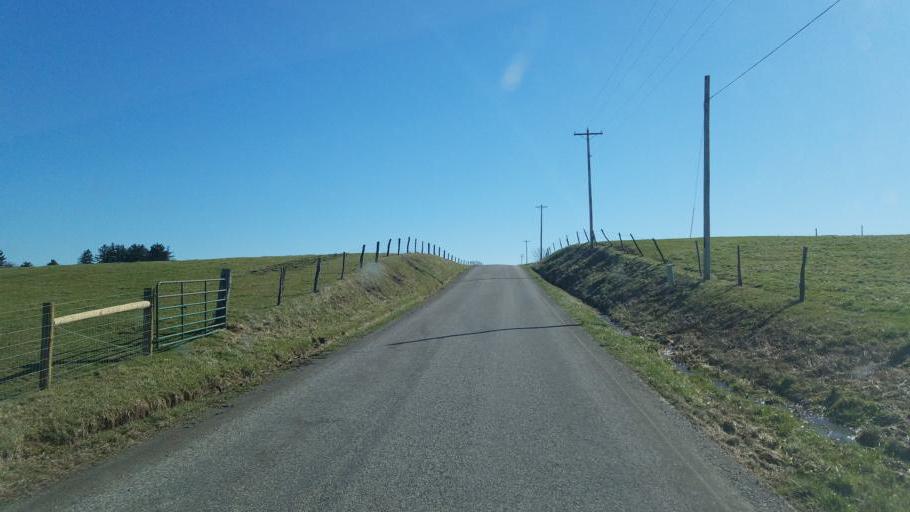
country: US
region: Ohio
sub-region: Wayne County
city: Apple Creek
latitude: 40.6530
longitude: -81.8358
